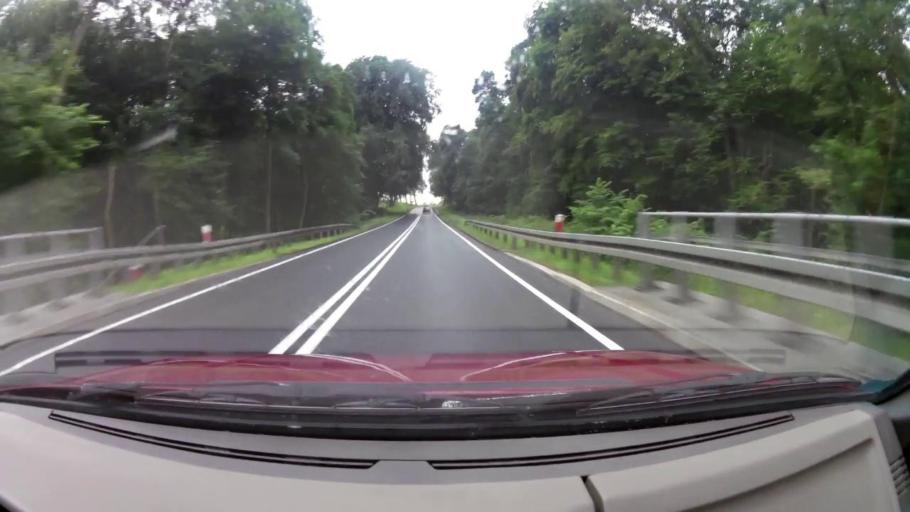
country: PL
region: West Pomeranian Voivodeship
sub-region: Powiat stargardzki
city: Marianowo
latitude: 53.4084
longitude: 15.2285
